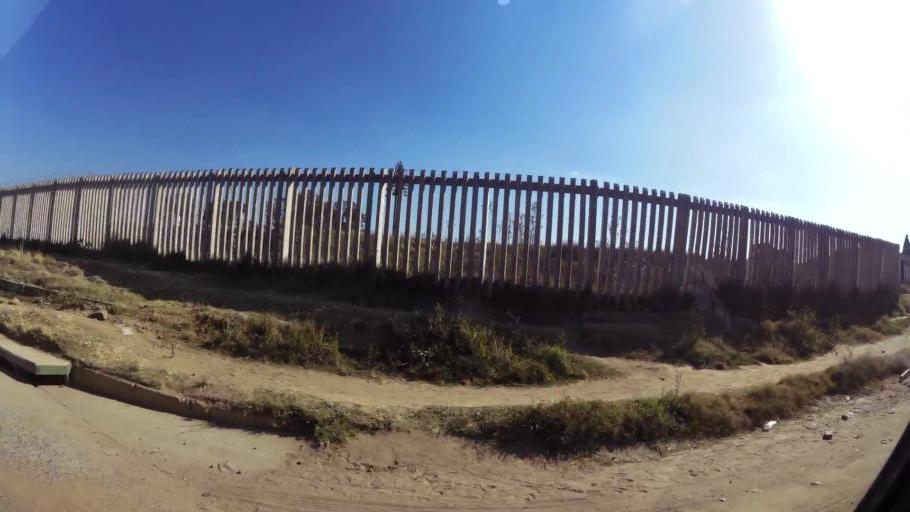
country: ZA
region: Gauteng
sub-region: West Rand District Municipality
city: Muldersdriseloop
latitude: -26.0197
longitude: 27.9292
